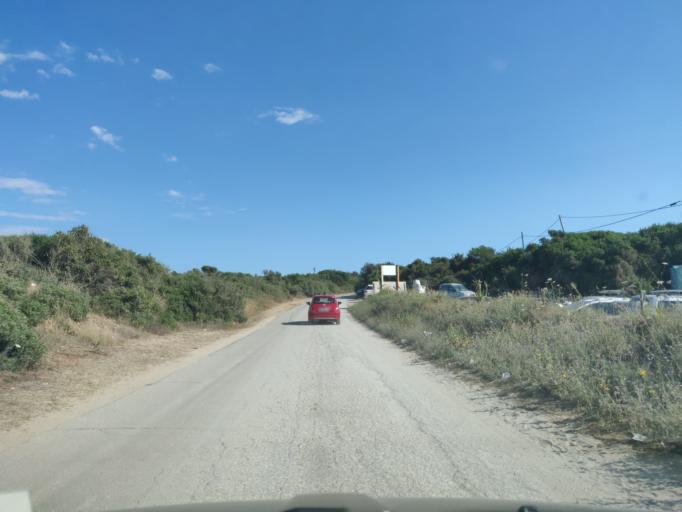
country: IT
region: Latium
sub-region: Citta metropolitana di Roma Capitale
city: Aurelia
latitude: 42.1710
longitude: 11.7409
